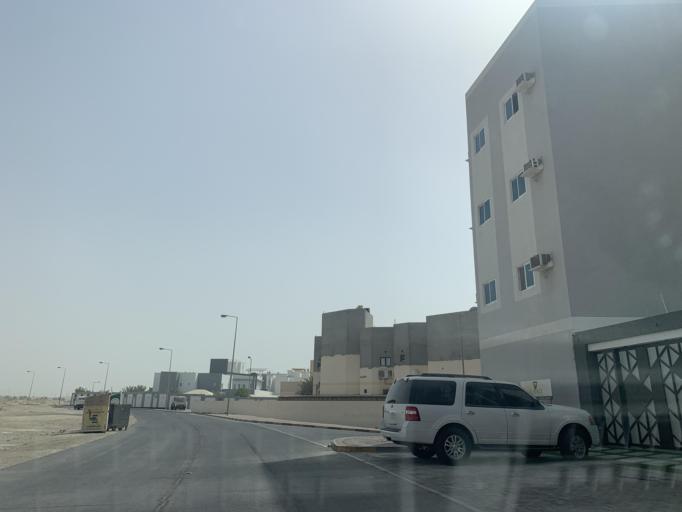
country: BH
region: Central Governorate
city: Madinat Hamad
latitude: 26.1550
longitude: 50.5117
